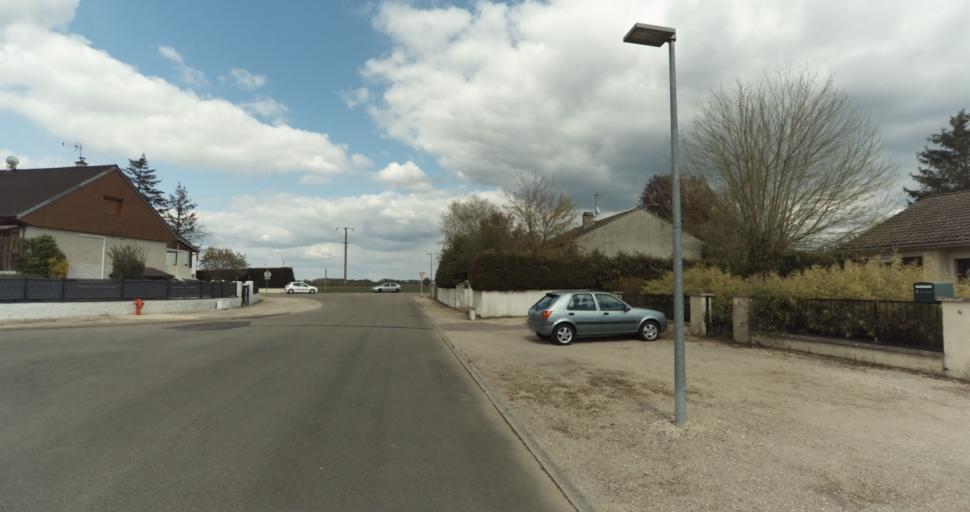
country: FR
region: Bourgogne
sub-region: Departement de la Cote-d'Or
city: Auxonne
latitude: 47.1960
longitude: 5.4134
